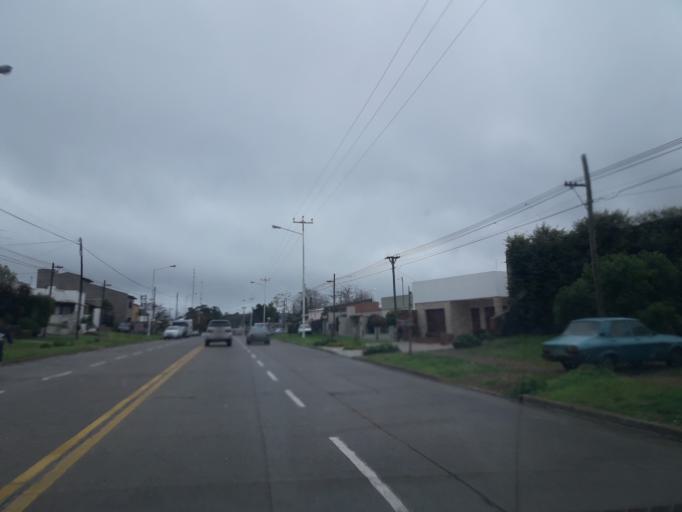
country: AR
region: Buenos Aires
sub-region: Partido de Tandil
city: Tandil
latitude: -37.3199
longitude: -59.1619
